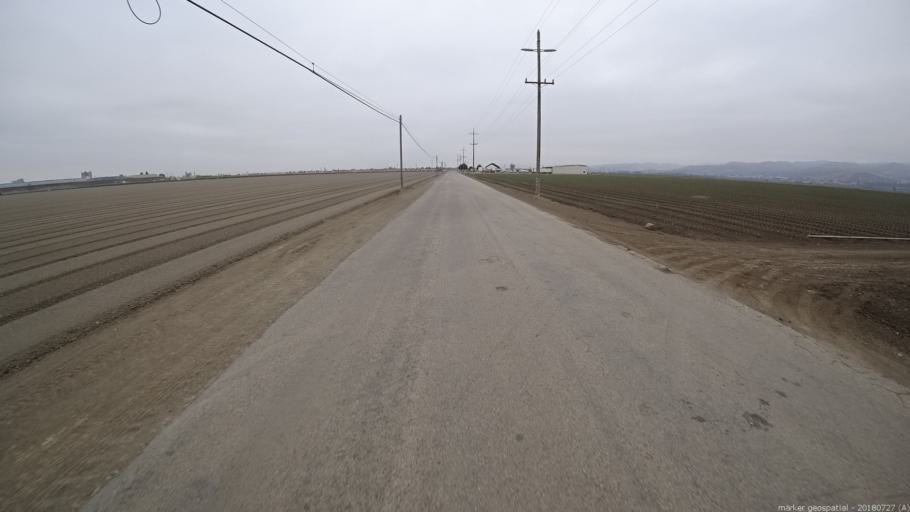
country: US
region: California
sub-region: Monterey County
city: King City
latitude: 36.2327
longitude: -121.1420
